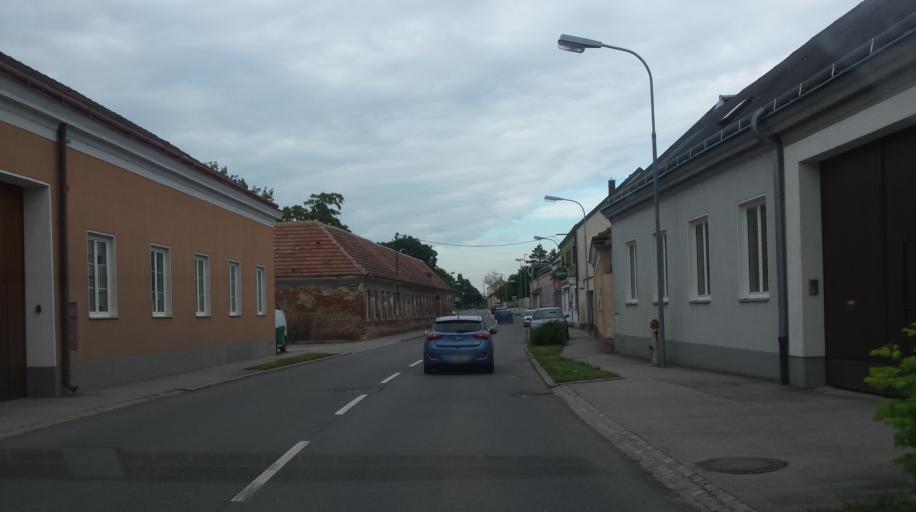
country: AT
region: Lower Austria
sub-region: Politischer Bezirk Wien-Umgebung
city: Zwolfaxing
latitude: 48.1077
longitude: 16.4610
